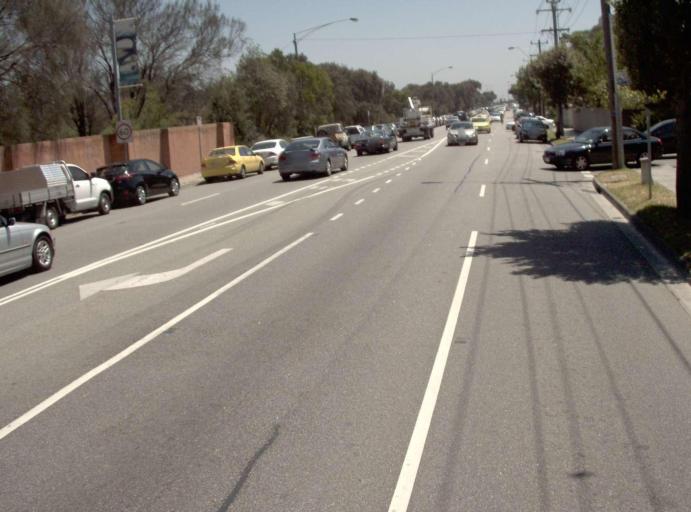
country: AU
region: Victoria
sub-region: Port Phillip
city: Elwood
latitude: -37.8873
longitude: 144.9844
